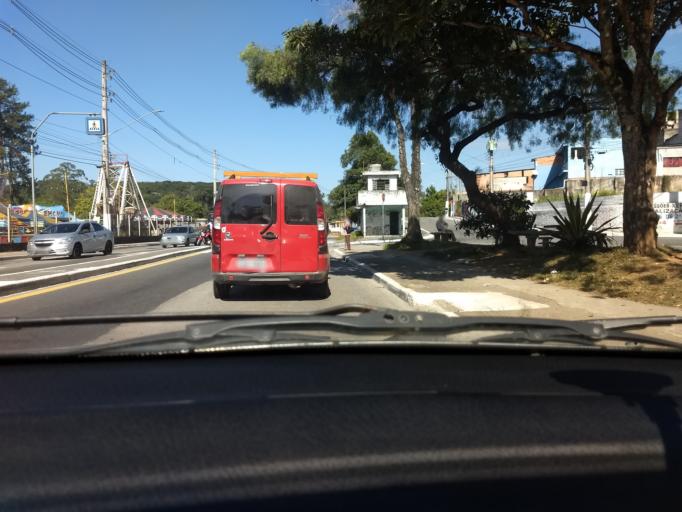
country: BR
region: Sao Paulo
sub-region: Embu-Guacu
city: Embu Guacu
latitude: -23.8113
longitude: -46.7366
